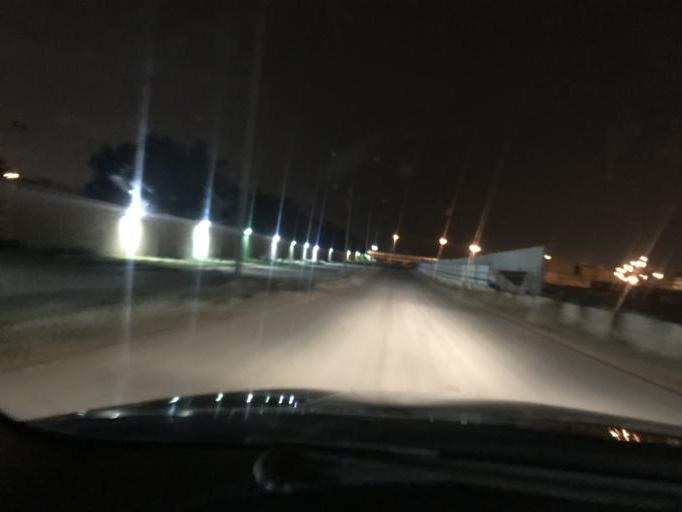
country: SA
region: Ar Riyad
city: Riyadh
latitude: 24.8129
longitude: 46.7169
